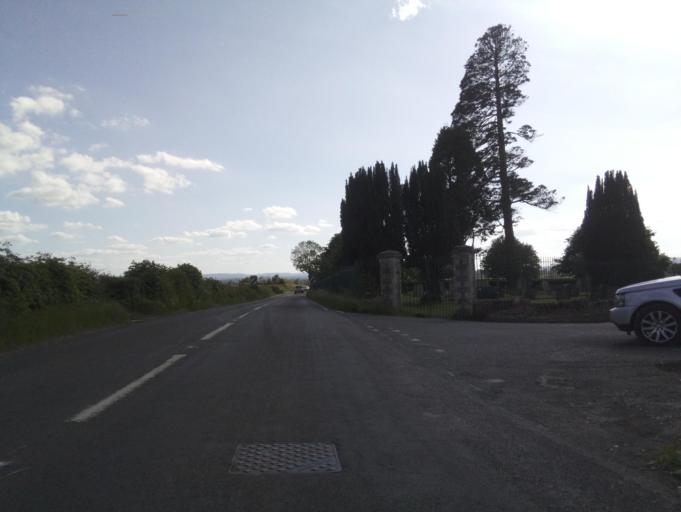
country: GB
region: England
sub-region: Somerset
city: Westonzoyland
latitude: 51.0773
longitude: -2.8898
